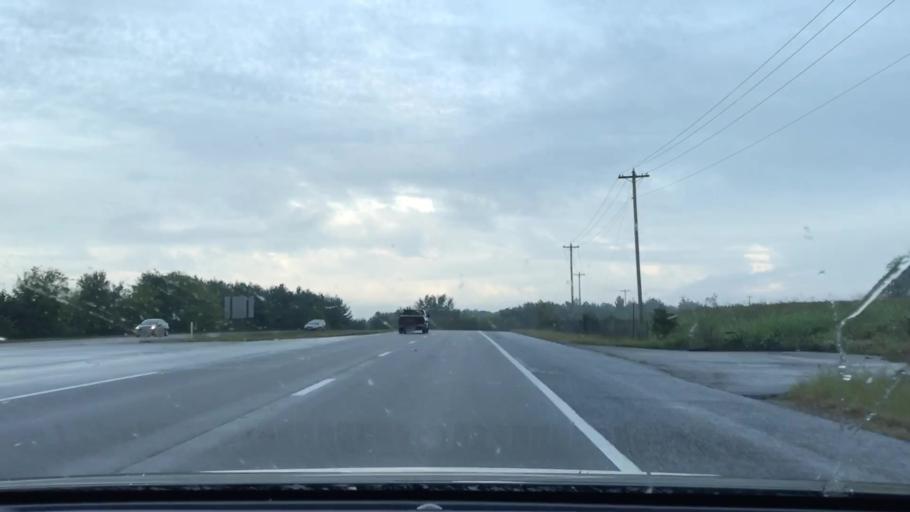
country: US
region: Tennessee
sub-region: Sumner County
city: Gallatin
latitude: 36.3934
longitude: -86.4791
